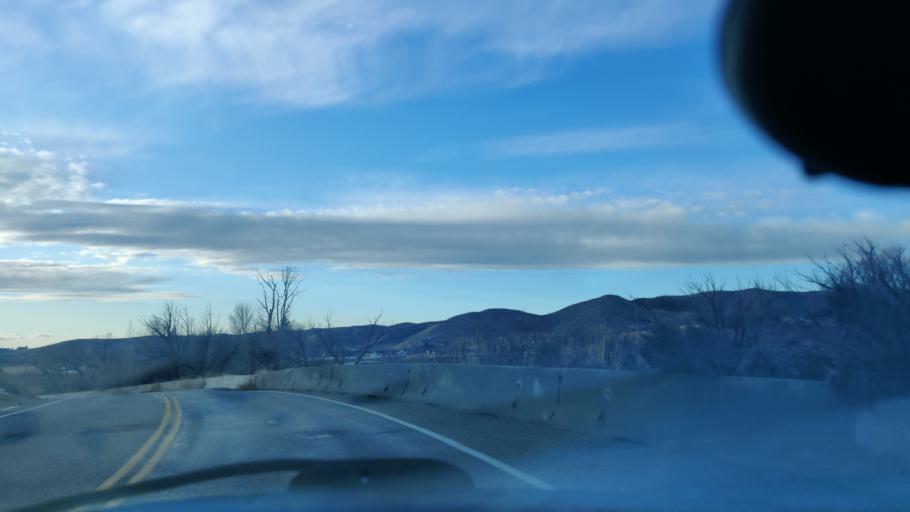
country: US
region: Idaho
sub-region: Ada County
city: Eagle
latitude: 43.7305
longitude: -116.2849
